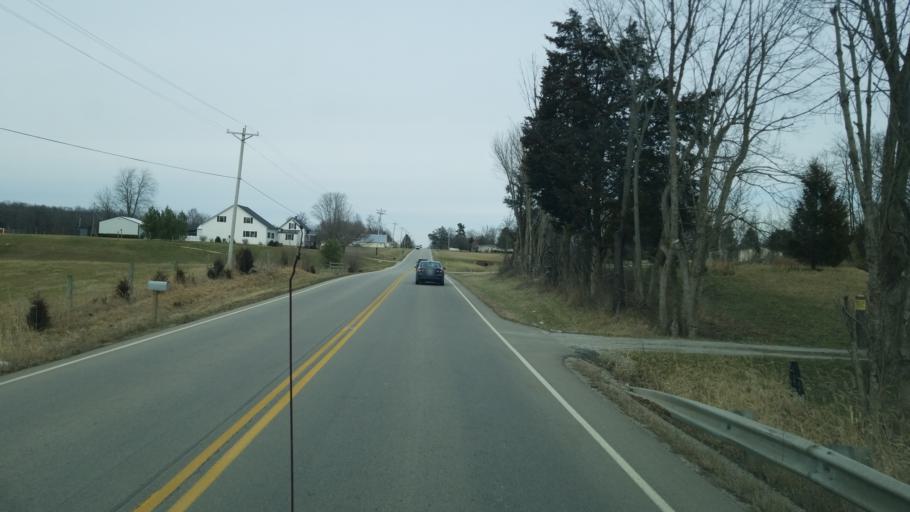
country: US
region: Ohio
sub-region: Adams County
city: Winchester
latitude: 39.0742
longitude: -83.6869
